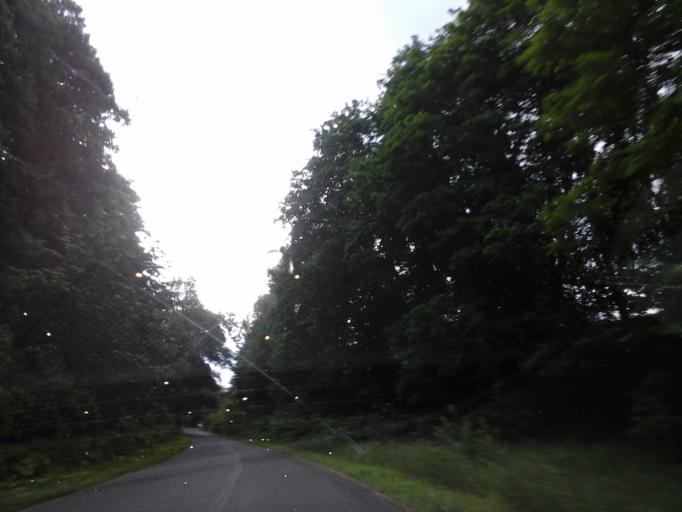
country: PL
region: West Pomeranian Voivodeship
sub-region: Powiat choszczenski
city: Drawno
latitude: 53.1800
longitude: 15.8561
